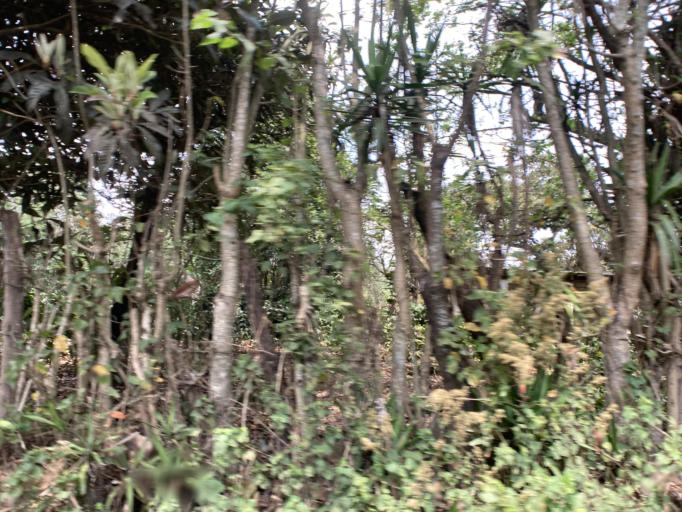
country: GT
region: Guatemala
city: Villa Canales
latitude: 14.4247
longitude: -90.5216
